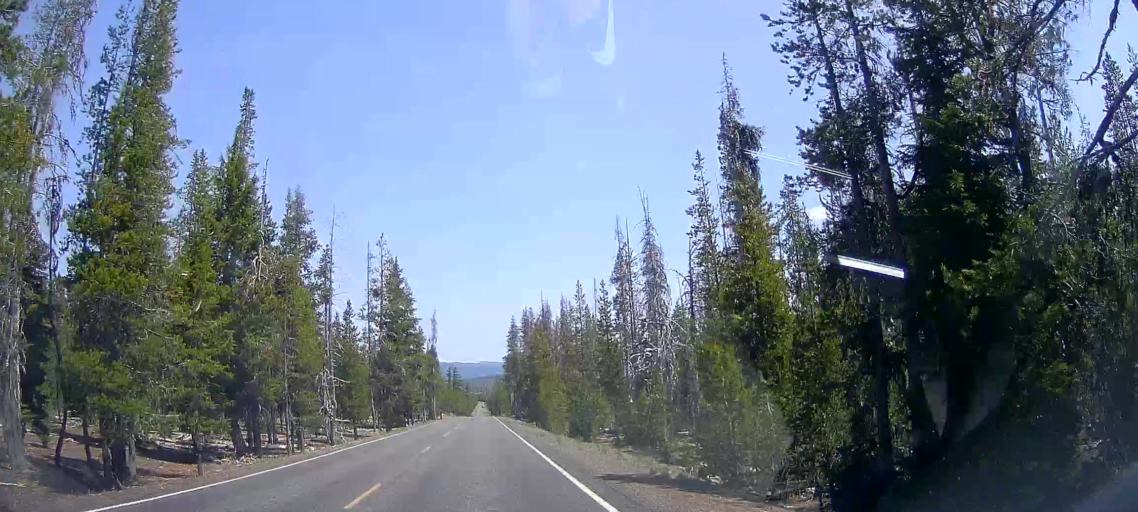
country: US
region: Oregon
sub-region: Jackson County
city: Shady Cove
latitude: 43.0142
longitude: -122.1278
